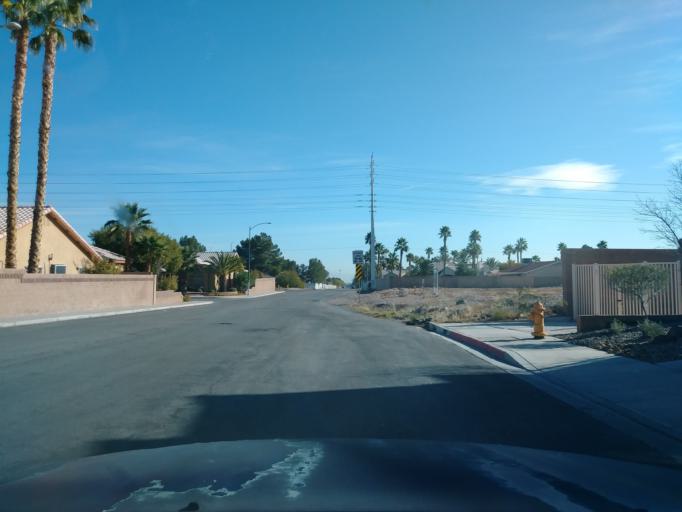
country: US
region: Nevada
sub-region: Clark County
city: Spring Valley
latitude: 36.1477
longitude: -115.2784
